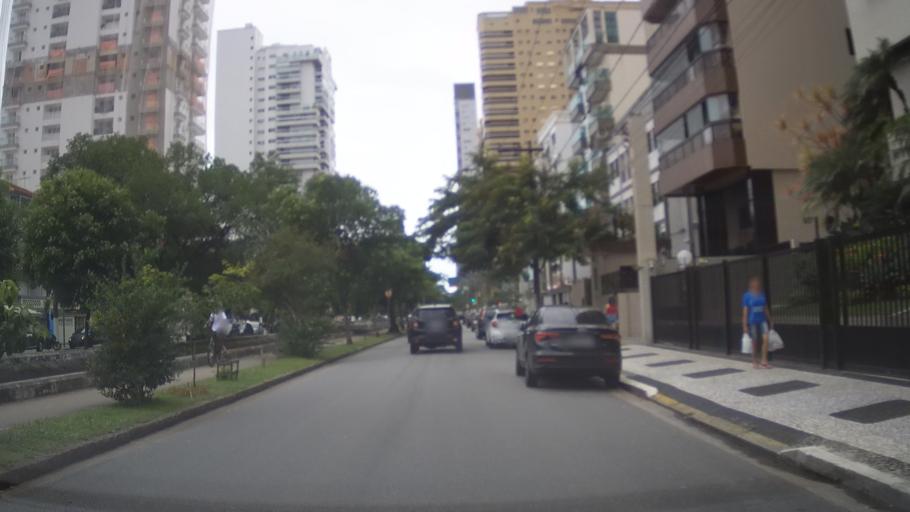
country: BR
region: Sao Paulo
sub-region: Santos
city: Santos
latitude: -23.9736
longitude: -46.3119
